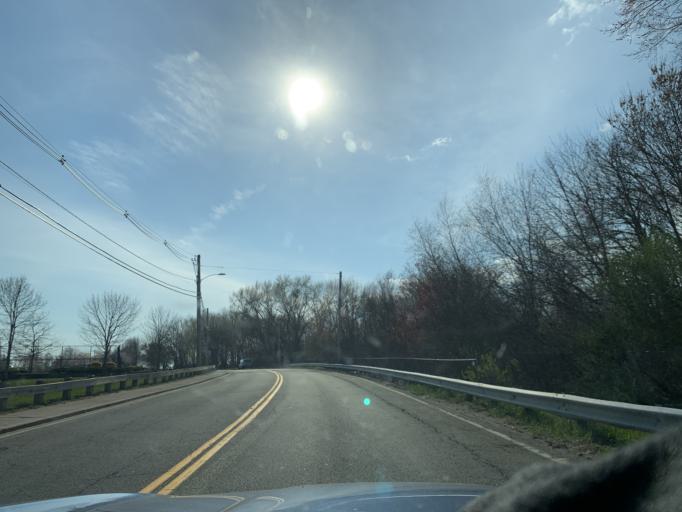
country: US
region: Rhode Island
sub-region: Kent County
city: West Warwick
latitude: 41.7545
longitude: -71.5109
